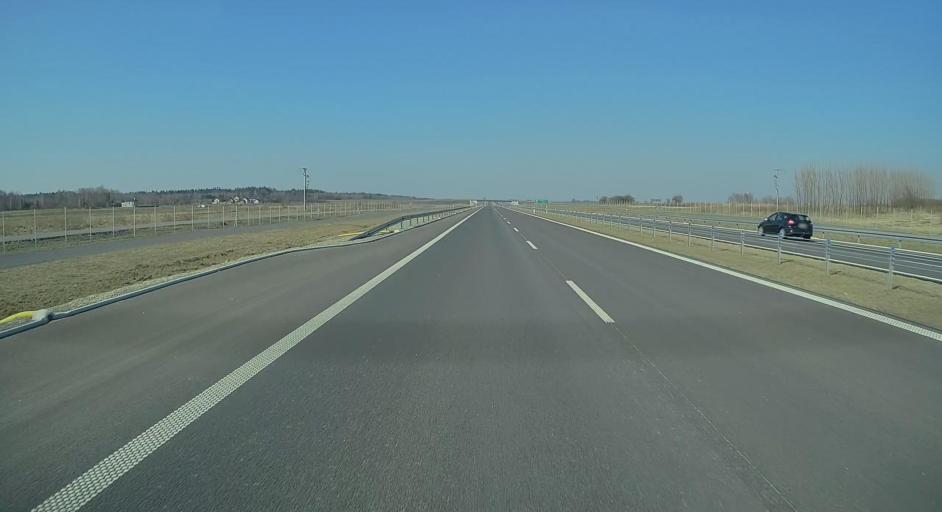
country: PL
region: Lublin Voivodeship
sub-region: Powiat janowski
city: Modliborzyce
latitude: 50.7390
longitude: 22.3283
